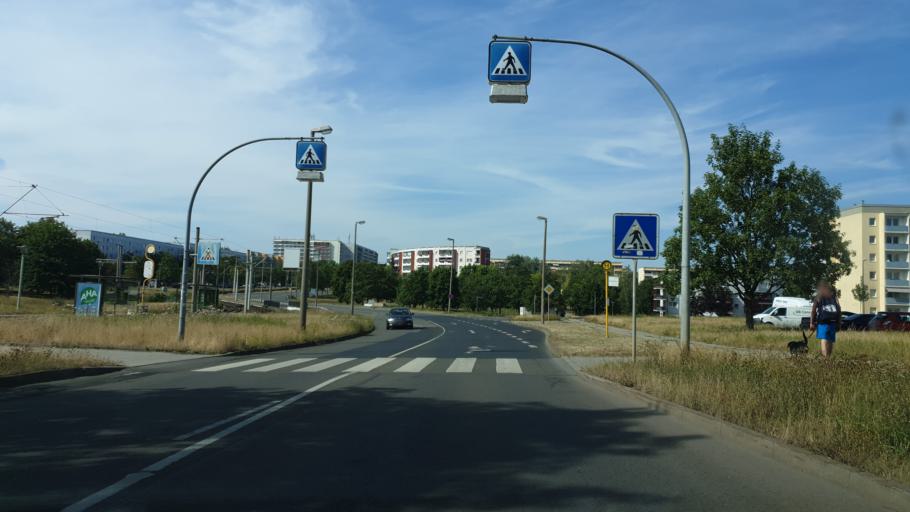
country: DE
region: Thuringia
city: Zedlitz
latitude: 50.8400
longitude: 12.0642
